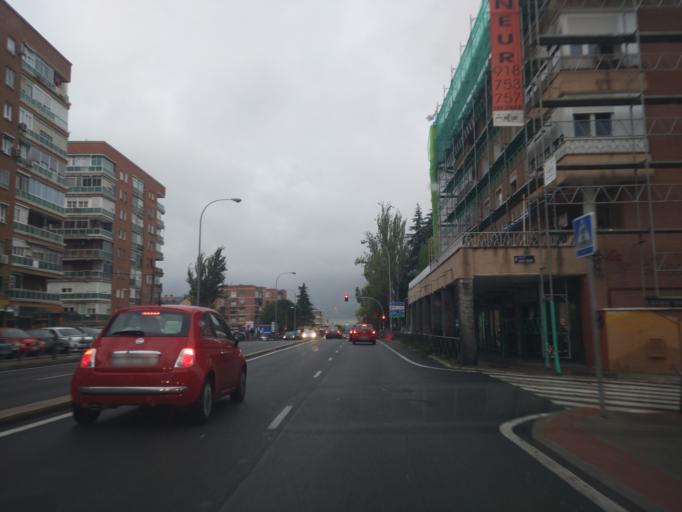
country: ES
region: Madrid
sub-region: Provincia de Madrid
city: Tetuan de las Victorias
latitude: 40.4806
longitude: -3.7221
